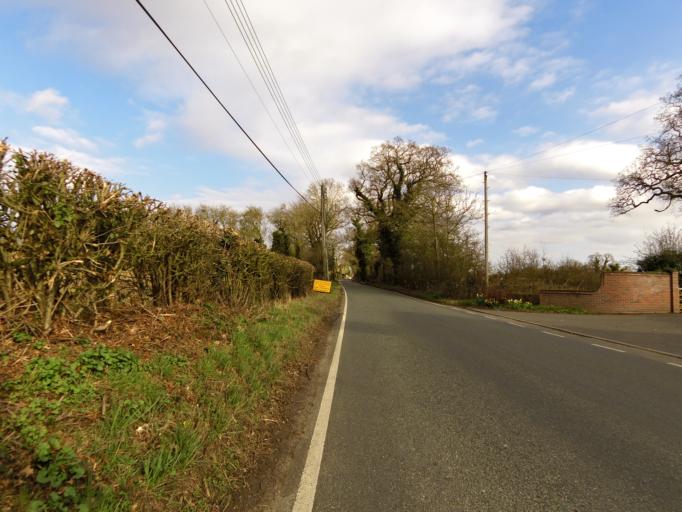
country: GB
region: England
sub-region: Suffolk
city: Ipswich
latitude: 52.0858
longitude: 1.1667
